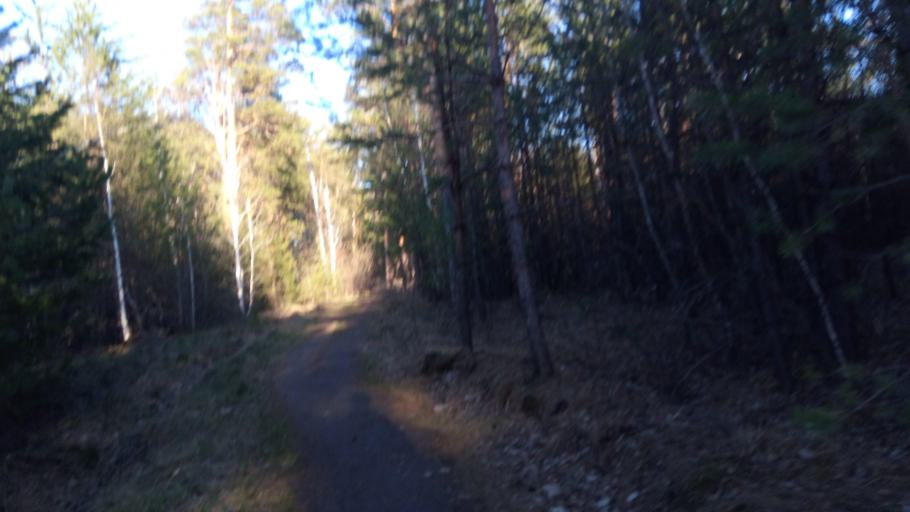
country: RU
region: Chelyabinsk
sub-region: Gorod Chelyabinsk
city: Chelyabinsk
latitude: 55.1386
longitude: 61.3340
